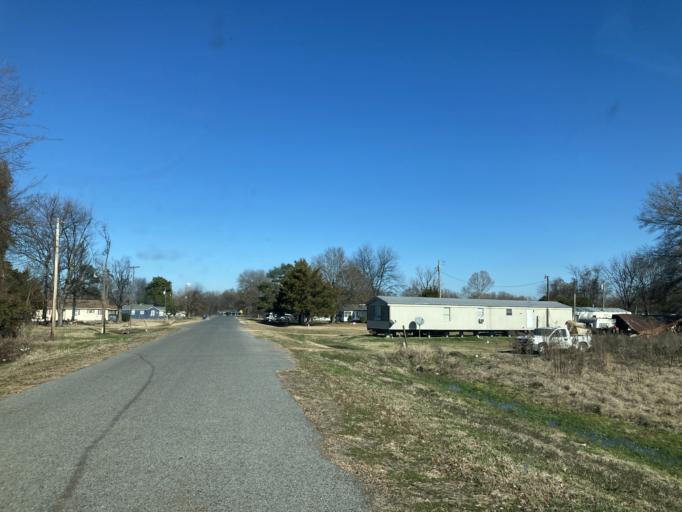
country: US
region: Mississippi
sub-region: Yazoo County
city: Yazoo City
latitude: 32.9751
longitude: -90.5941
